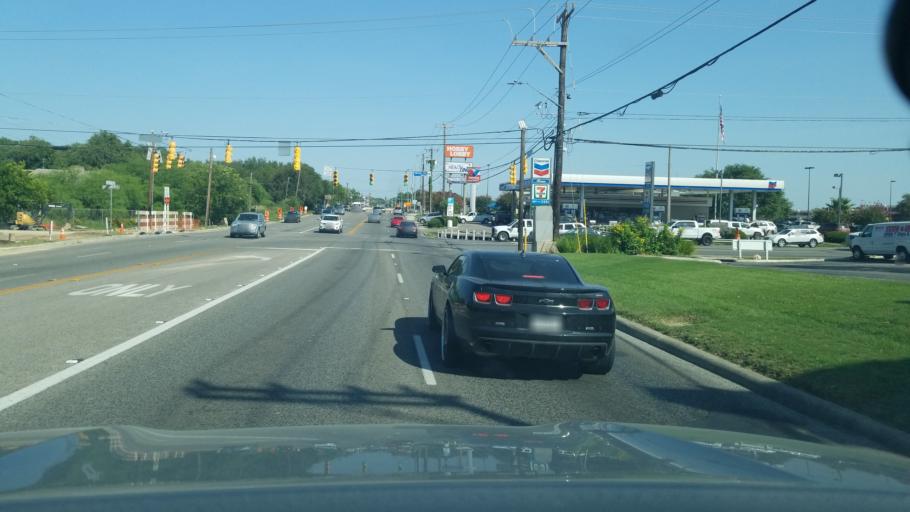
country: US
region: Texas
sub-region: Bexar County
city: Hollywood Park
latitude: 29.5685
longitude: -98.4872
